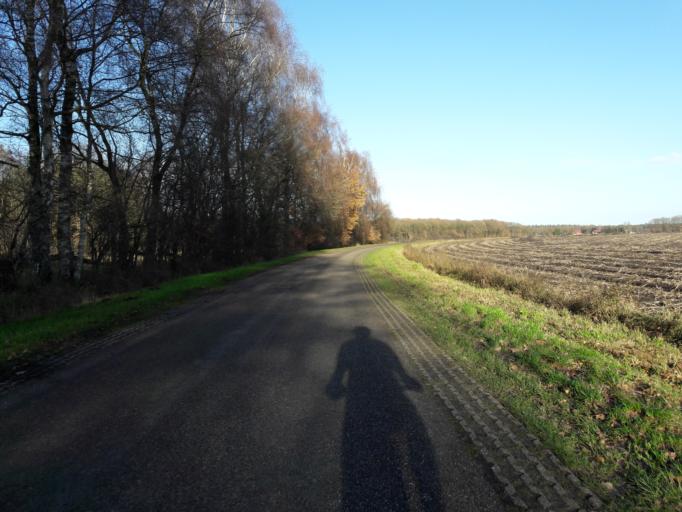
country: NL
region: Drenthe
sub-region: Gemeente Borger-Odoorn
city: Borger
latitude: 52.9088
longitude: 6.7028
